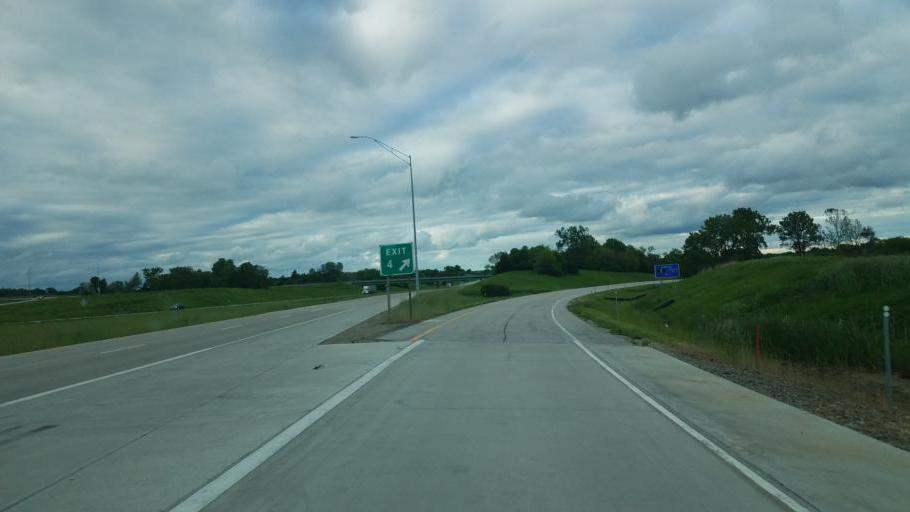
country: US
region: Iowa
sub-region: Decatur County
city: Lamoni
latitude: 40.6199
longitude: -93.8931
